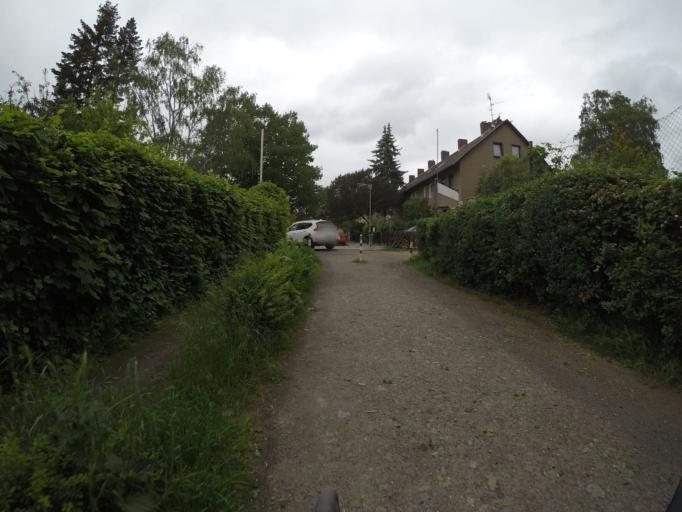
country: DE
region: Berlin
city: Tegel
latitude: 52.5959
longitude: 13.2966
